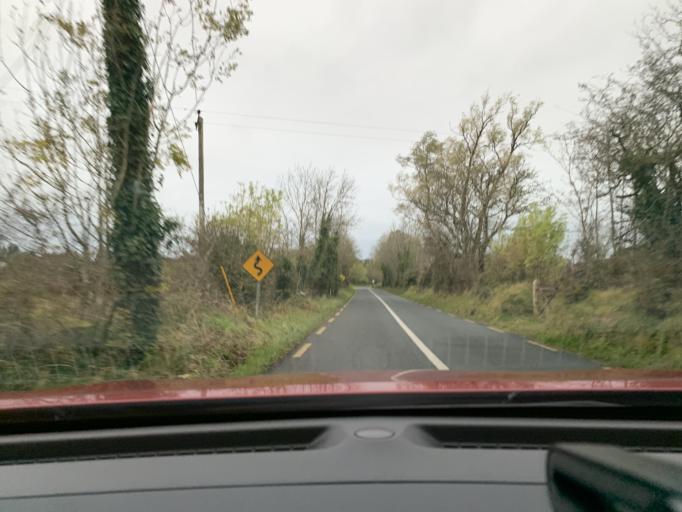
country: IE
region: Connaught
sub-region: Sligo
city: Ballymote
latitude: 54.0596
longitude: -8.5133
